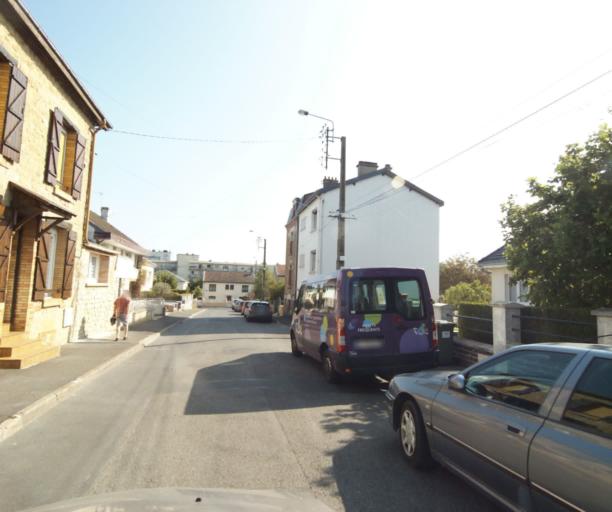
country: FR
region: Champagne-Ardenne
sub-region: Departement des Ardennes
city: Charleville-Mezieres
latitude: 49.7785
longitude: 4.7102
